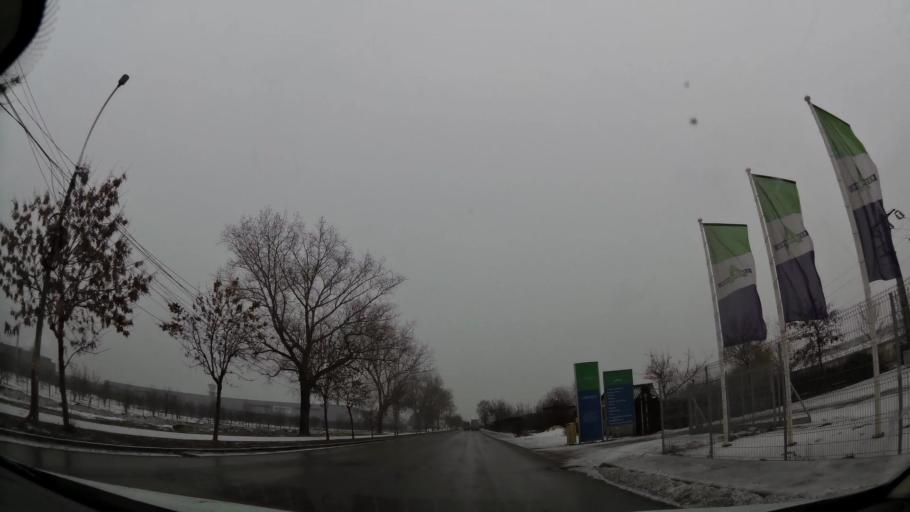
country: RO
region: Dambovita
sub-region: Municipiul Targoviste
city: Targoviste
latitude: 44.9202
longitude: 25.4353
